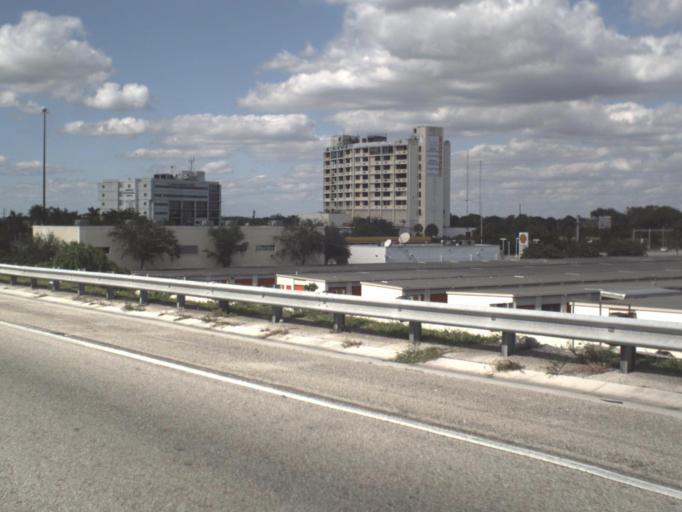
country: US
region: Florida
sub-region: Miami-Dade County
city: Golden Glades
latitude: 25.9288
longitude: -80.2094
